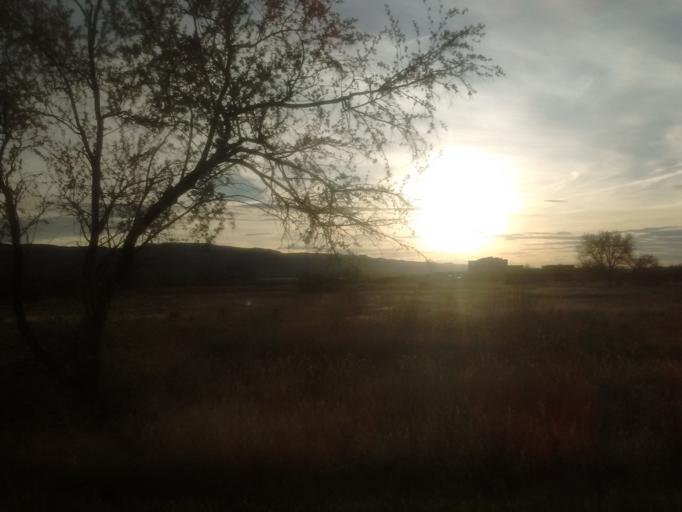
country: US
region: Colorado
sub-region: Mesa County
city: Redlands
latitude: 39.1041
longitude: -108.6082
